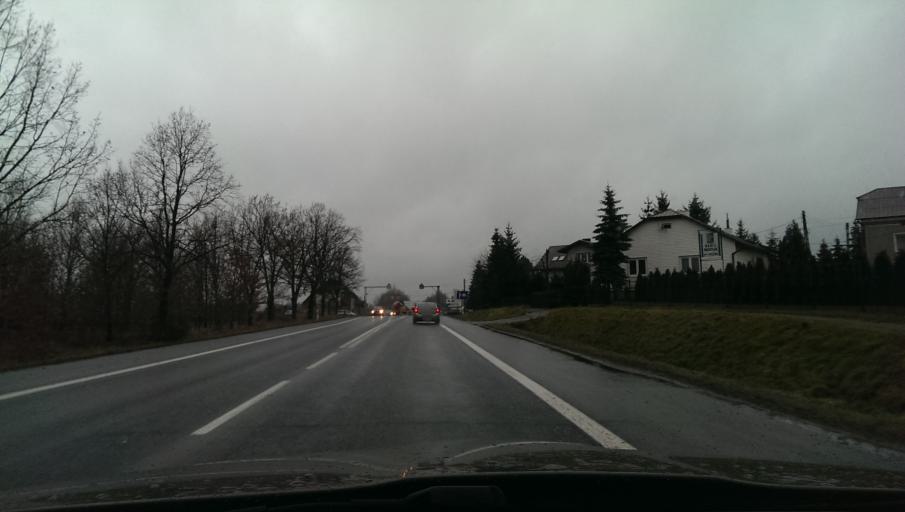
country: PL
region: Subcarpathian Voivodeship
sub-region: Powiat rzeszowski
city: Rudna Mala
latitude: 50.0945
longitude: 21.9805
